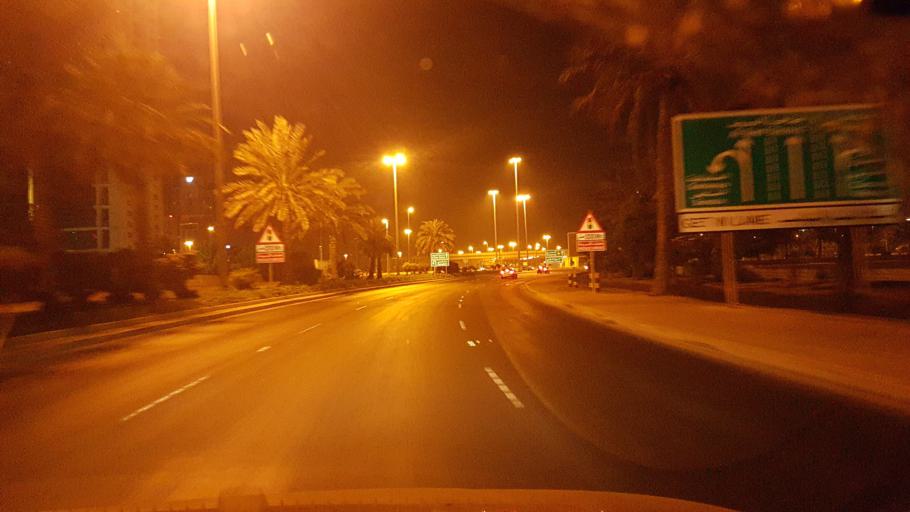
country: BH
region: Manama
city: Jidd Hafs
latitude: 26.2281
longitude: 50.5609
